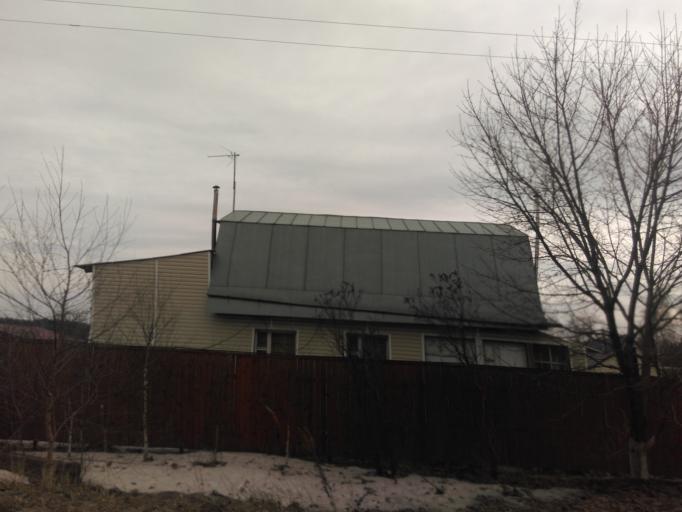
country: RU
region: Moskovskaya
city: Kolyubakino
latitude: 55.6929
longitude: 36.5763
